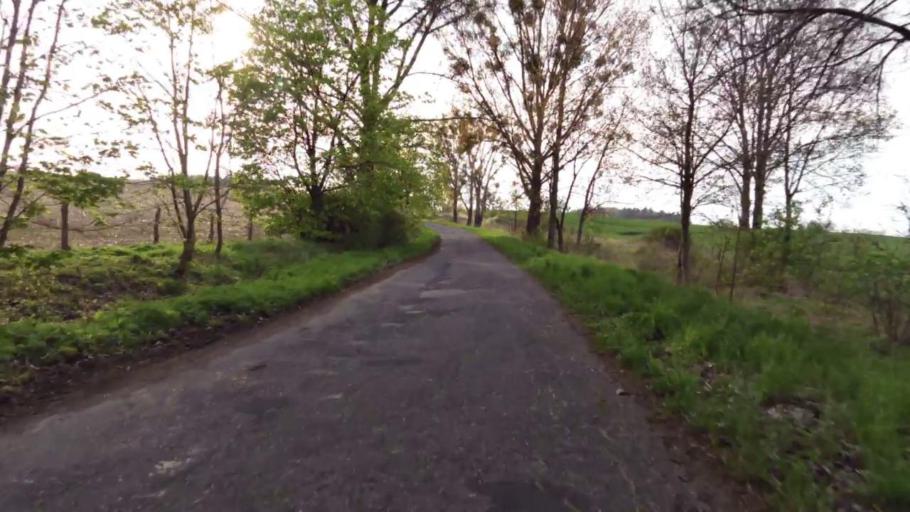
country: PL
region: West Pomeranian Voivodeship
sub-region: Powiat mysliborski
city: Mysliborz
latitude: 52.8942
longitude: 14.7803
